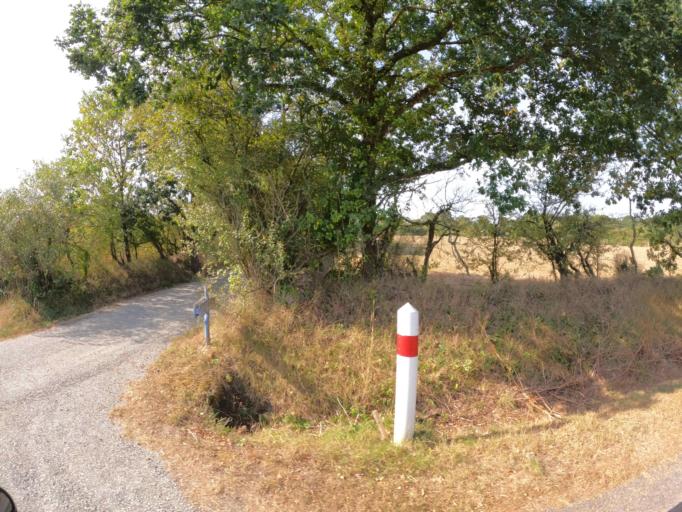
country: FR
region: Pays de la Loire
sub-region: Departement de la Vendee
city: Challans
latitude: 46.8076
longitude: -1.8520
